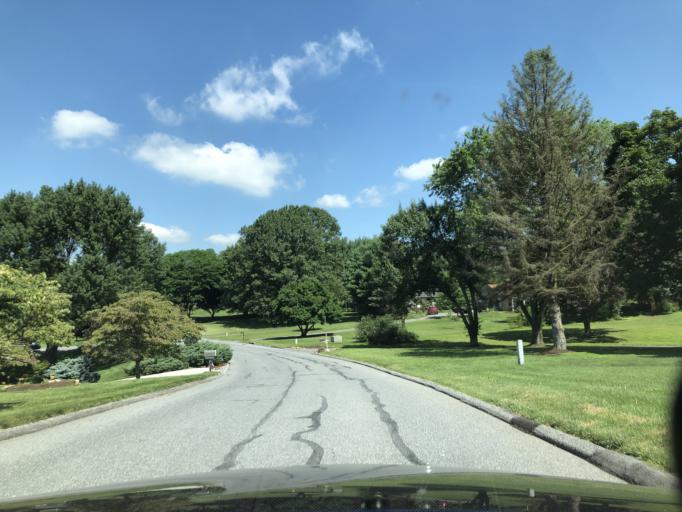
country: US
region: Maryland
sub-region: Carroll County
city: Westminster
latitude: 39.6183
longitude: -76.9987
